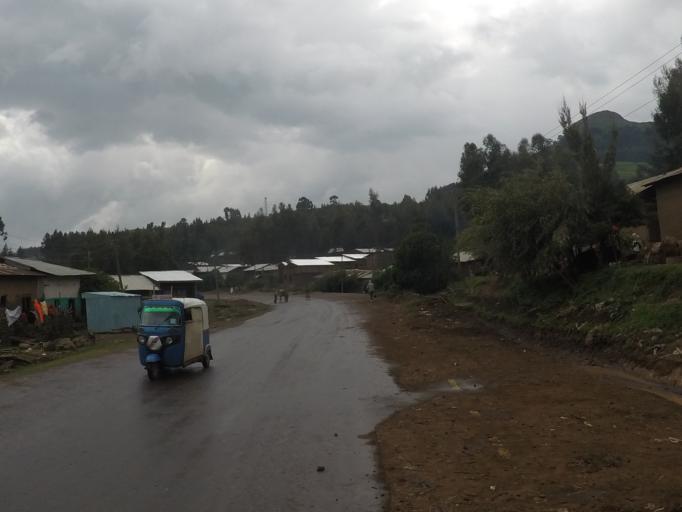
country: ET
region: Amhara
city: Dabat
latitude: 13.0652
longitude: 37.8244
